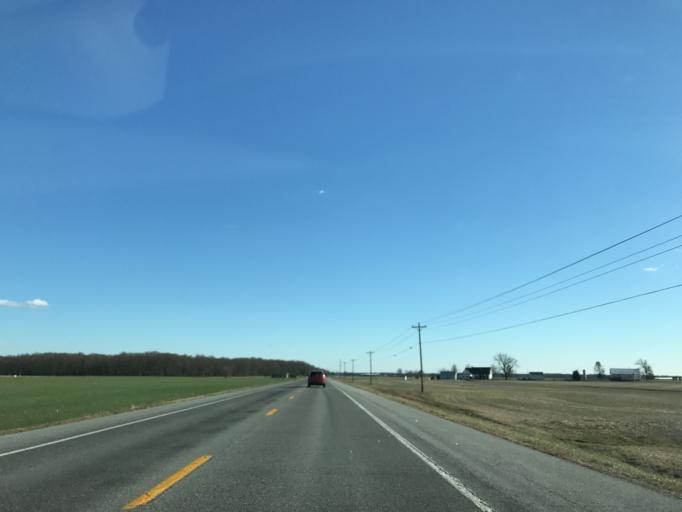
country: US
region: Maryland
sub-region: Caroline County
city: Greensboro
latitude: 39.0970
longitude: -75.8714
